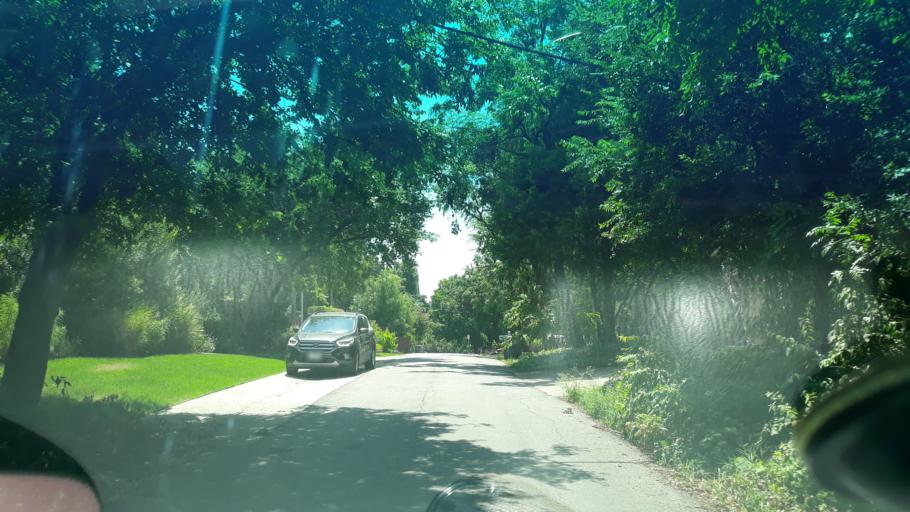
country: US
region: Texas
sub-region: Dallas County
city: Highland Park
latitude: 32.8298
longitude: -96.7314
